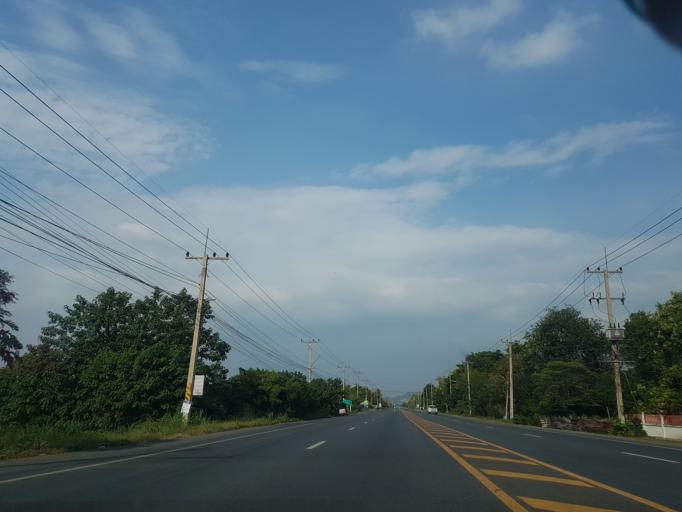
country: TH
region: Sara Buri
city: Ban Mo
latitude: 14.6355
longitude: 100.7533
